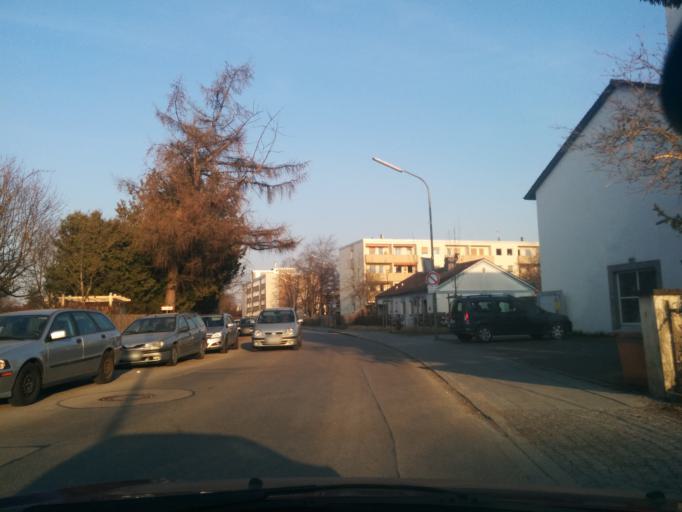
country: DE
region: Bavaria
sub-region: Upper Bavaria
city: Germering
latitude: 48.1272
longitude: 11.3673
